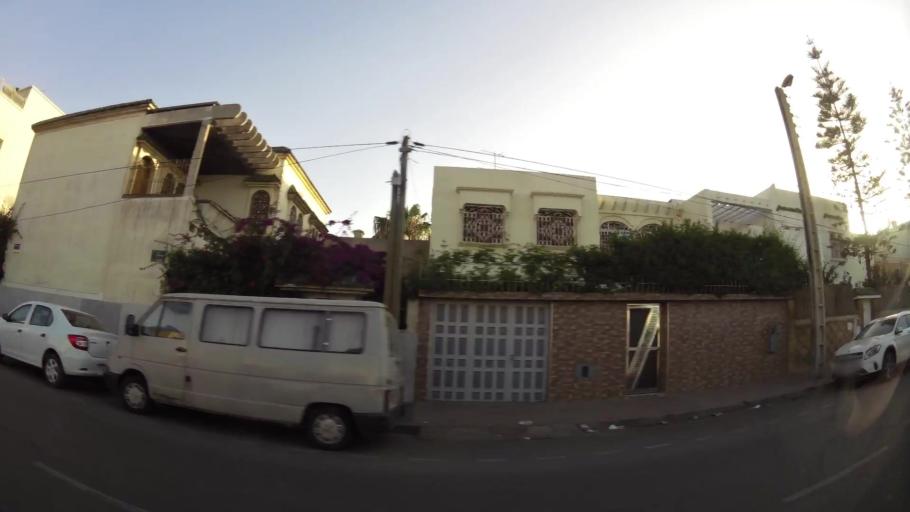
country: MA
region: Oued ed Dahab-Lagouira
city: Dakhla
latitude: 30.4146
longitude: -9.5598
